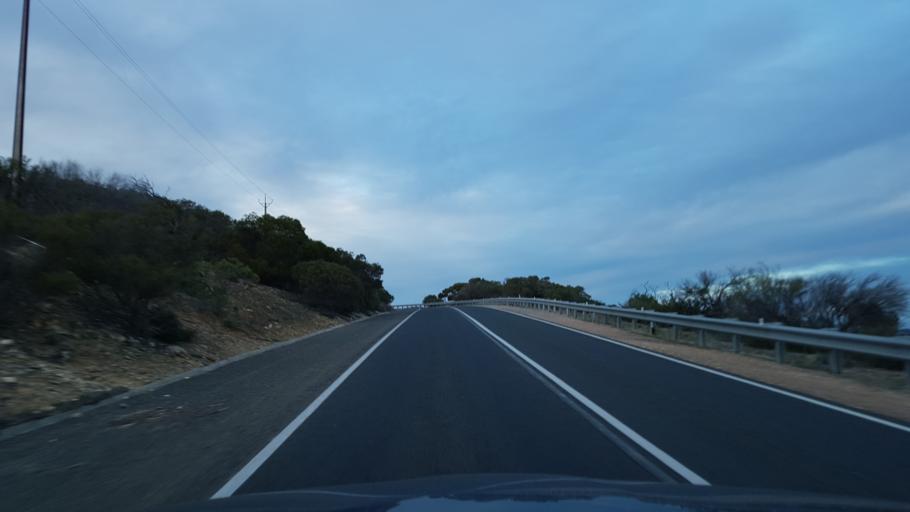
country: AU
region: South Australia
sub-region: Mid Murray
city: Mannum
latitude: -34.7537
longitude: 139.5718
